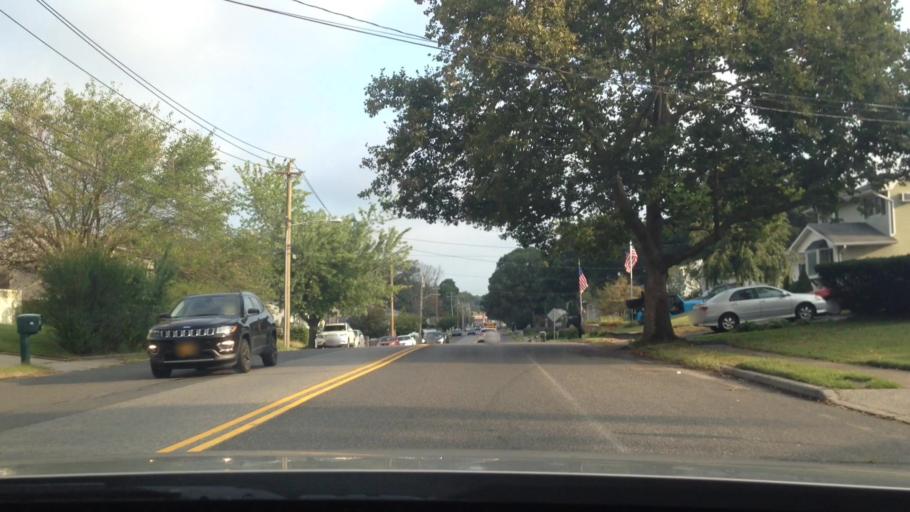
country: US
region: New York
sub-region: Suffolk County
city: Selden
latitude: 40.8585
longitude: -73.0468
